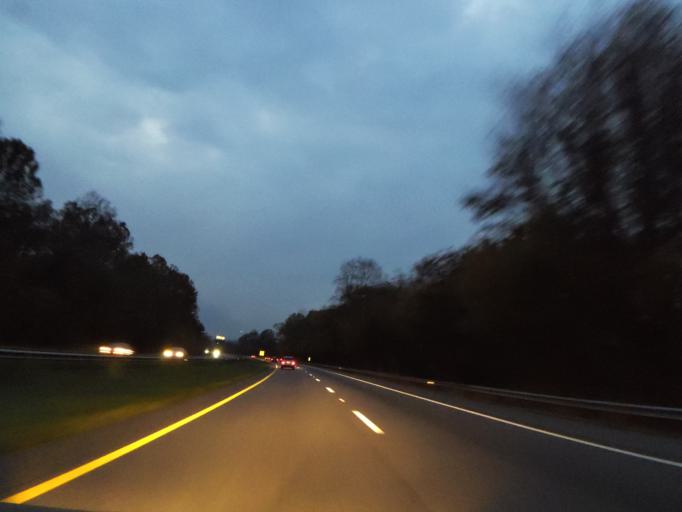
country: US
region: North Carolina
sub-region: McDowell County
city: West Marion
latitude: 35.6376
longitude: -82.1599
